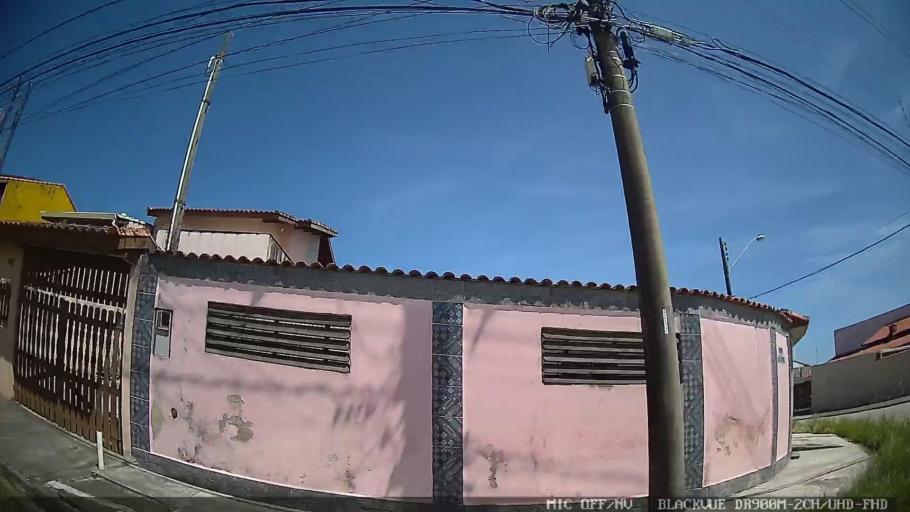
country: BR
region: Sao Paulo
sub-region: Peruibe
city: Peruibe
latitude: -24.3003
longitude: -46.9933
